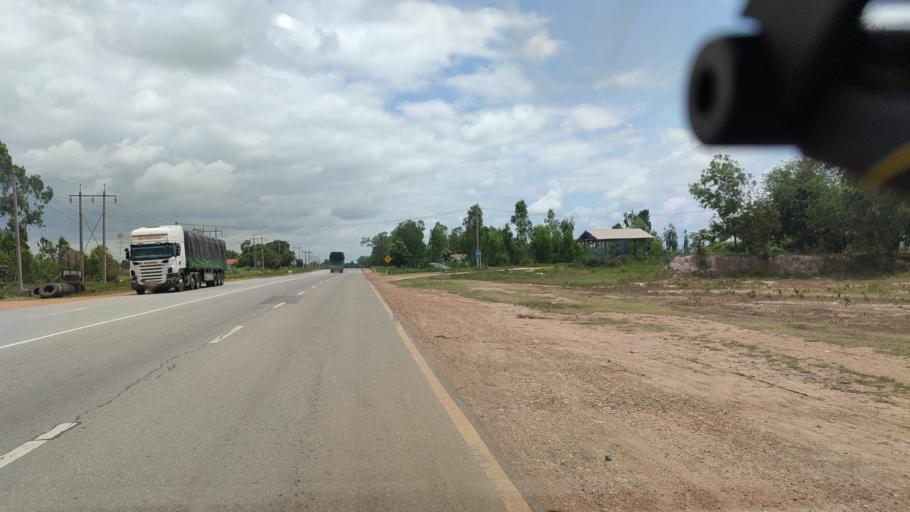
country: MM
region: Mandalay
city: Pyinmana
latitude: 19.5633
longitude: 96.2465
